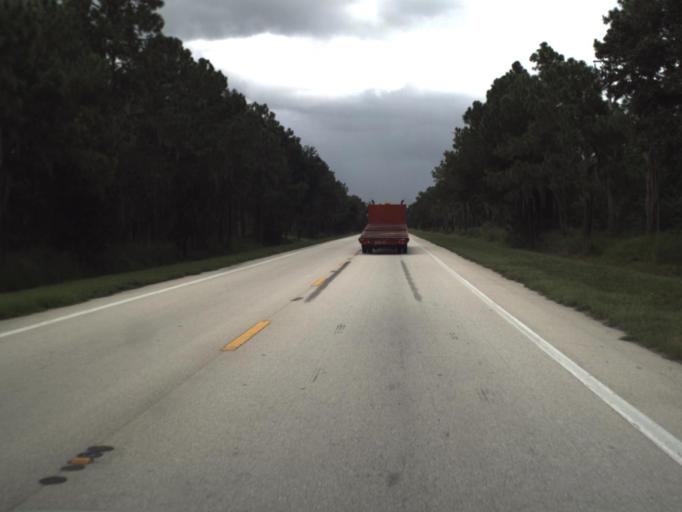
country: US
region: Florida
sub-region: Polk County
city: Mulberry
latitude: 27.7083
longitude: -82.0181
